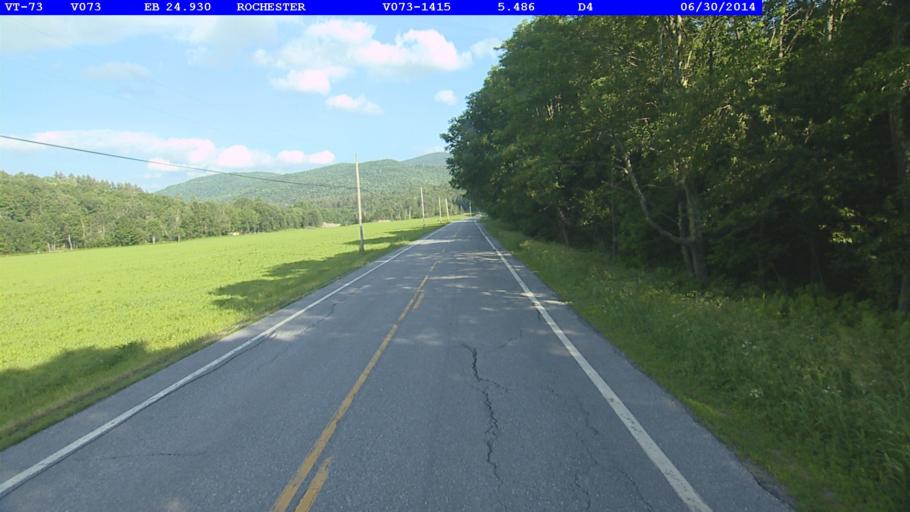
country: US
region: Vermont
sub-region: Orange County
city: Randolph
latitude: 43.8534
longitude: -72.8642
